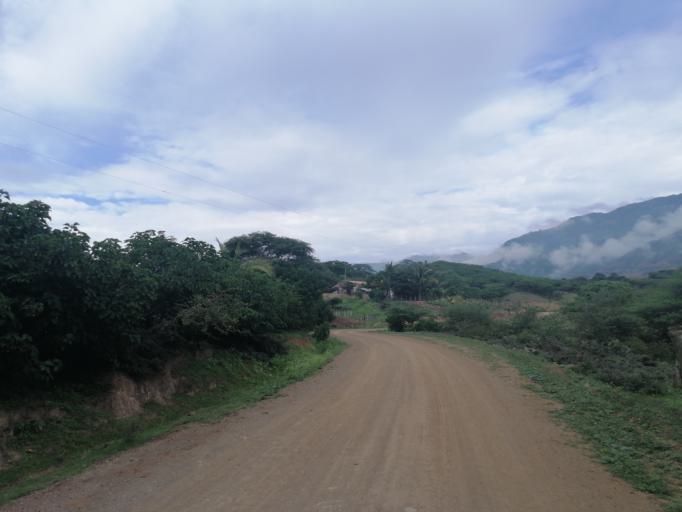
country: EC
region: Loja
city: Catacocha
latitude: -4.0110
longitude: -79.6912
